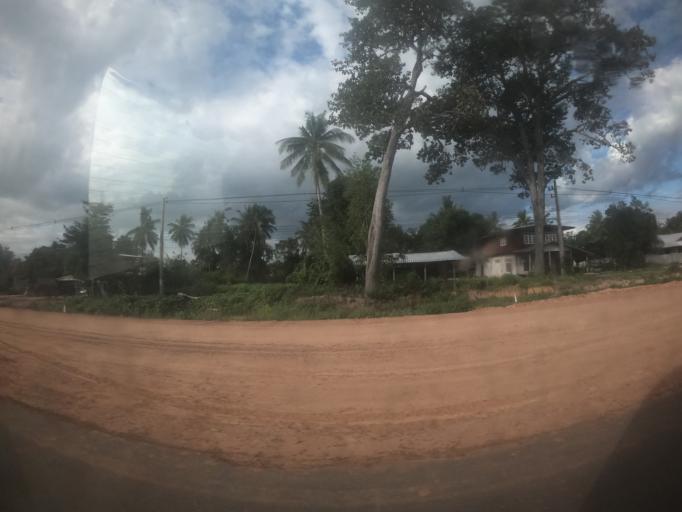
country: TH
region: Surin
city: Kap Choeng
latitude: 14.4893
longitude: 103.5755
